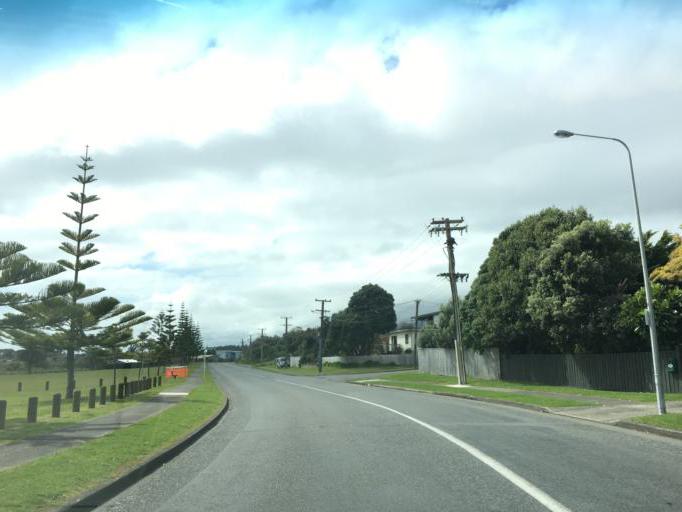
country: NZ
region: Wellington
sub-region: Kapiti Coast District
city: Paraparaumu
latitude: -40.8700
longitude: 175.0195
